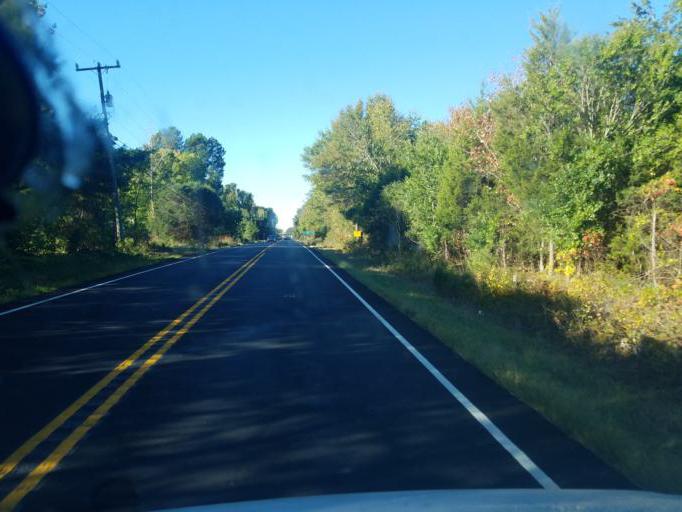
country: US
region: Virginia
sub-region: Fauquier County
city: Bealeton
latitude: 38.5667
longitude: -77.7958
